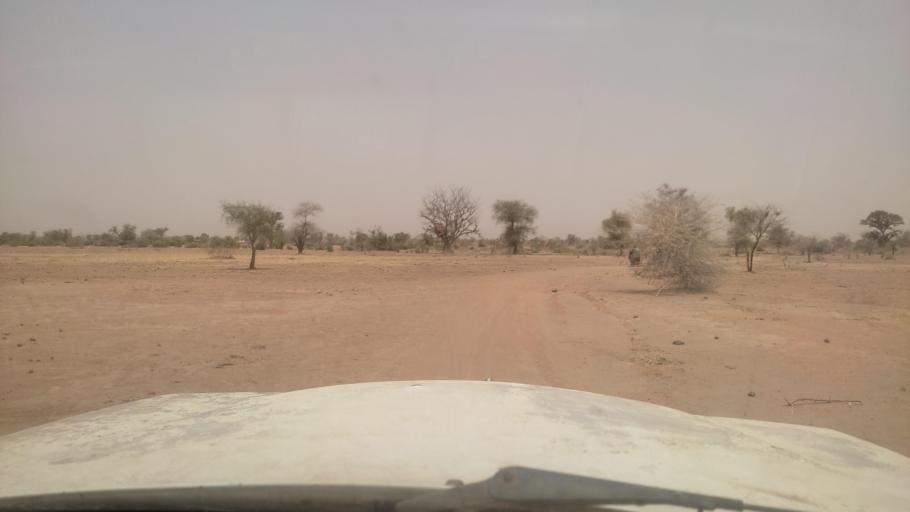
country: BF
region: Est
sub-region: Gnagna Province
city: Bogande
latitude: 13.0343
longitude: -0.0740
